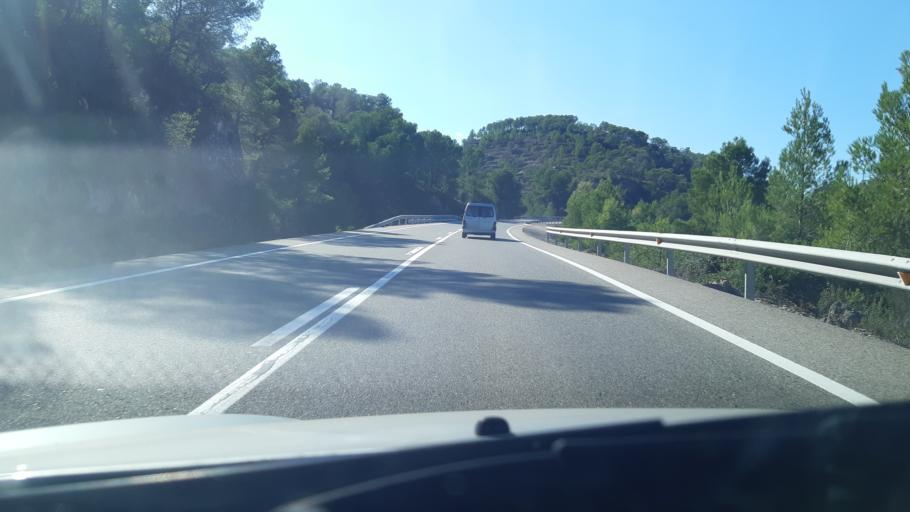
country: ES
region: Catalonia
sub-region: Provincia de Tarragona
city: Rasquera
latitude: 41.0026
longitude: 0.5896
